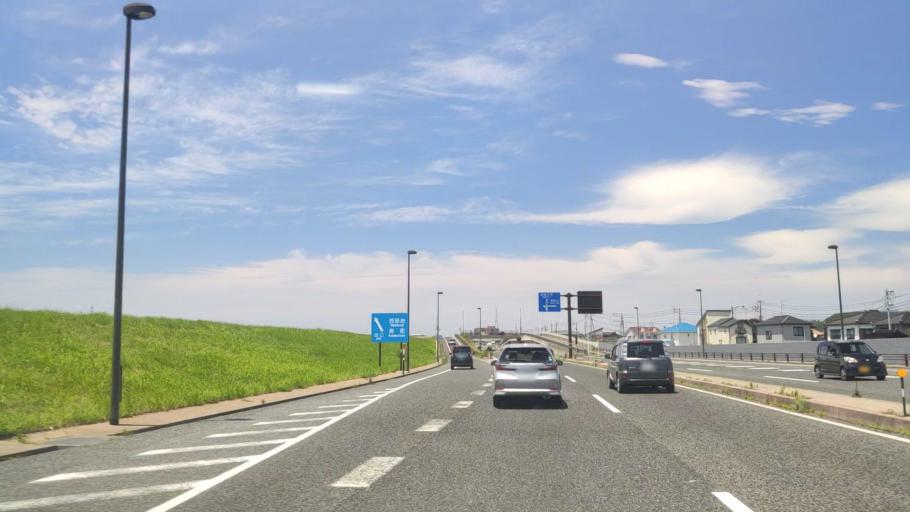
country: JP
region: Tottori
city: Tottori
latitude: 35.5025
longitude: 134.2180
